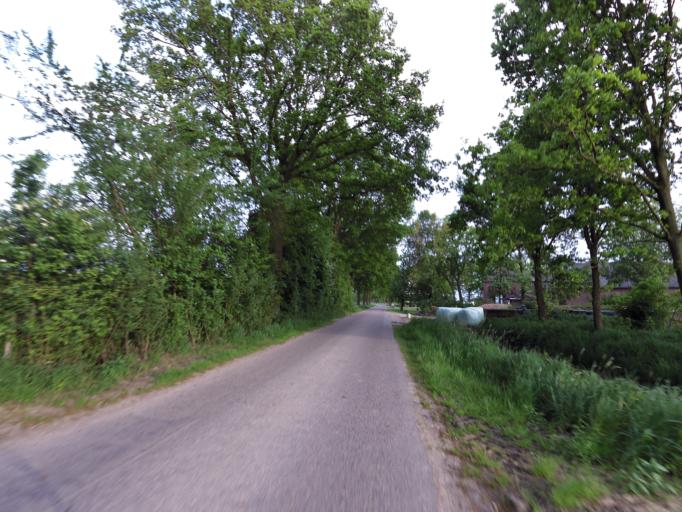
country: NL
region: Gelderland
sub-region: Oude IJsselstreek
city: Gendringen
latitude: 51.8593
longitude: 6.3674
